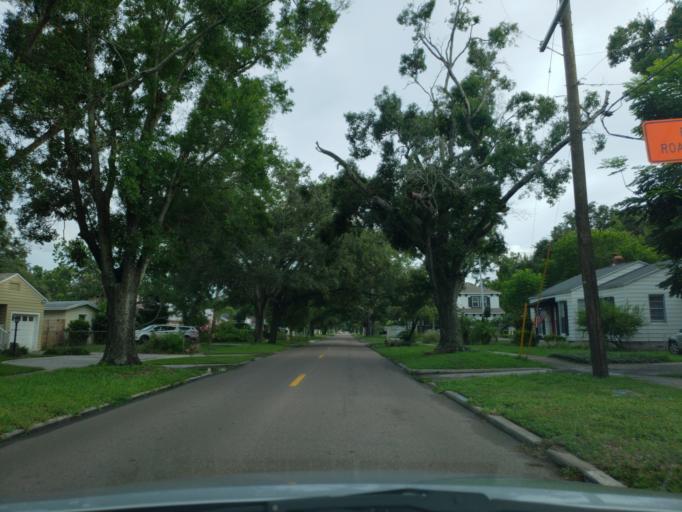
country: US
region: Florida
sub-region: Hillsborough County
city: Tampa
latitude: 27.9435
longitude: -82.5016
